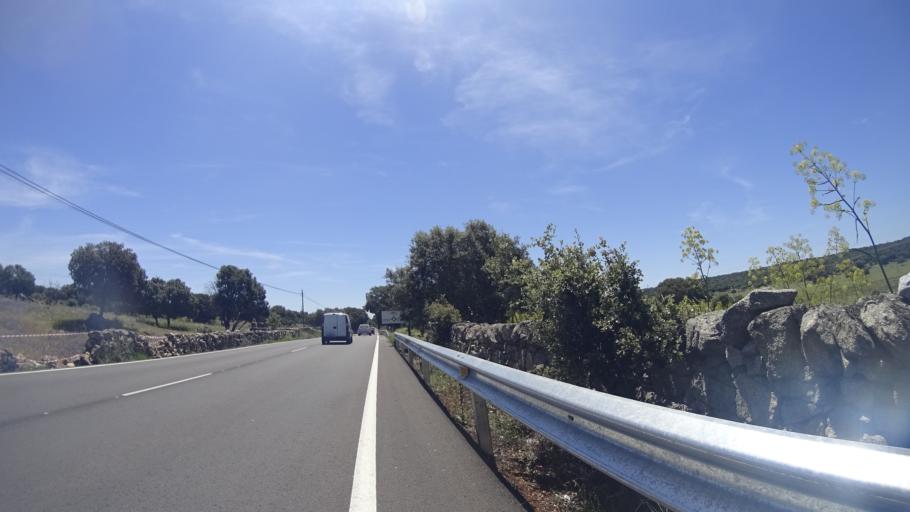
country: ES
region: Madrid
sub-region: Provincia de Madrid
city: Galapagar
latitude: 40.5954
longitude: -4.0150
